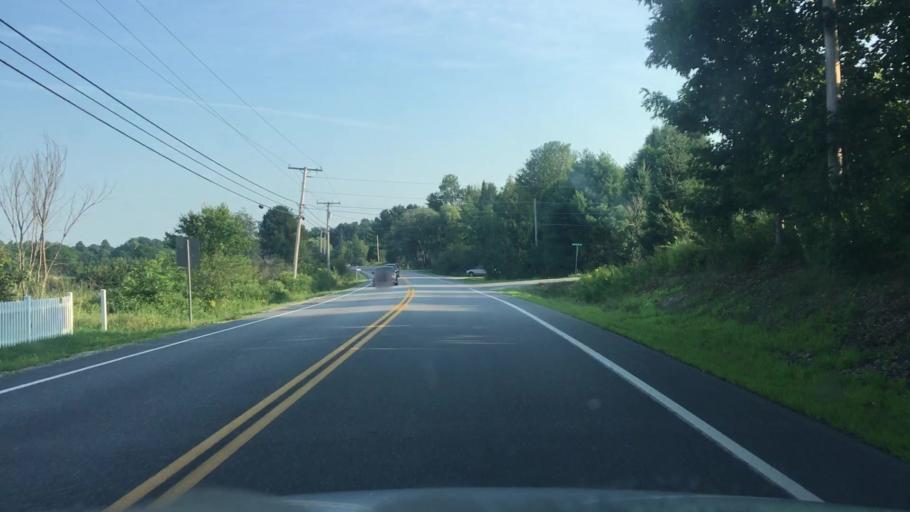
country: US
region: Maine
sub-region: Cumberland County
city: Freeport
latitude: 43.8954
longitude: -70.0948
